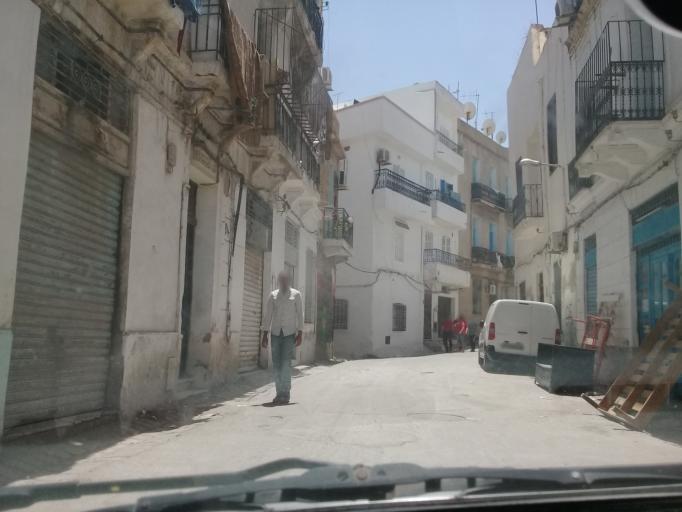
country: TN
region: Tunis
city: Tunis
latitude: 36.7918
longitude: 10.1794
